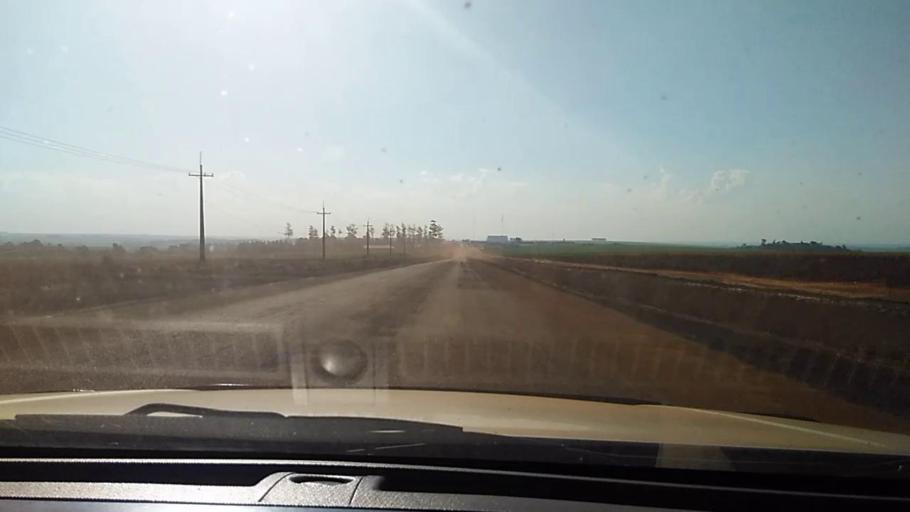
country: PY
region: Alto Parana
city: Naranjal
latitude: -25.9132
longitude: -55.4399
